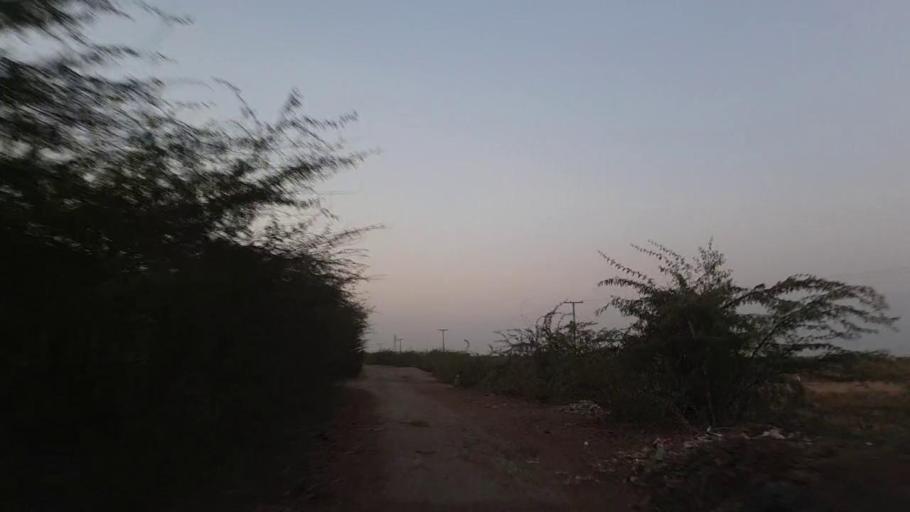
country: PK
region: Sindh
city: Naukot
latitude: 24.8885
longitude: 69.3851
